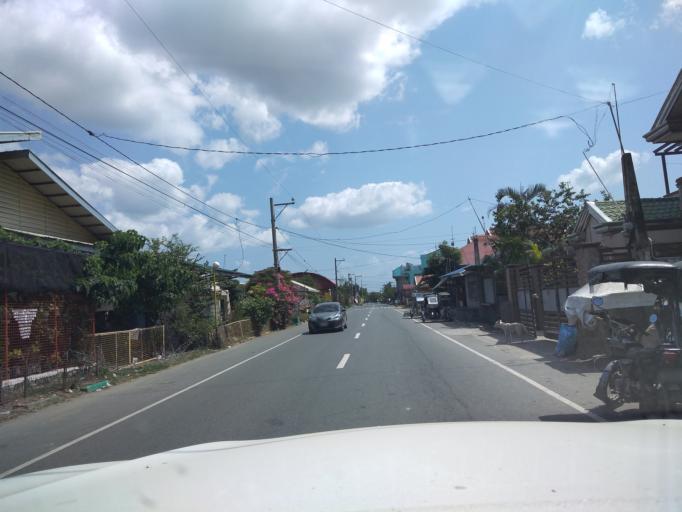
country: PH
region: Central Luzon
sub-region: Province of Pampanga
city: Bahay Pare
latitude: 15.0478
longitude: 120.8775
